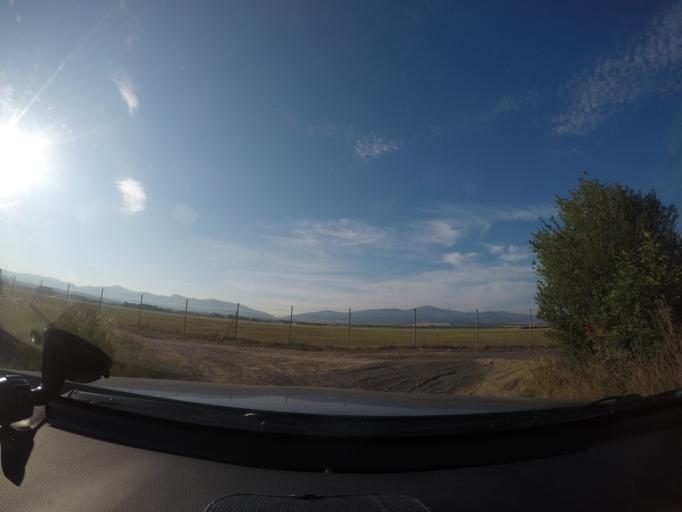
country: SK
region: Trenciansky
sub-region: Okres Trencin
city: Trencin
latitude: 48.8728
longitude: 18.0038
